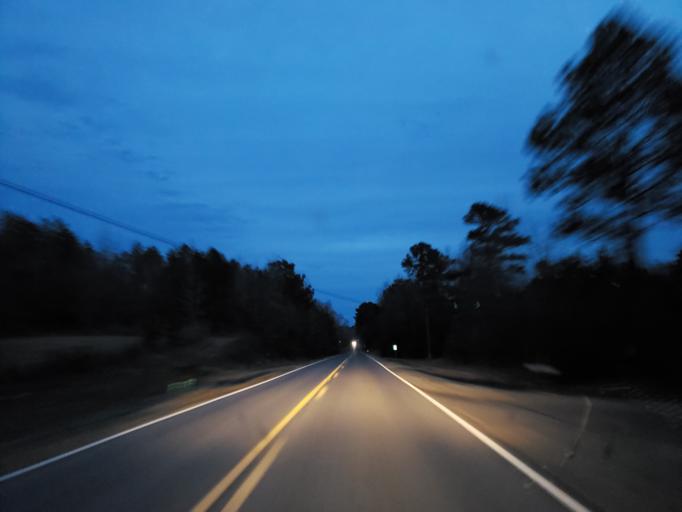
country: US
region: Alabama
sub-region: Greene County
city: Eutaw
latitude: 32.8849
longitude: -87.9400
